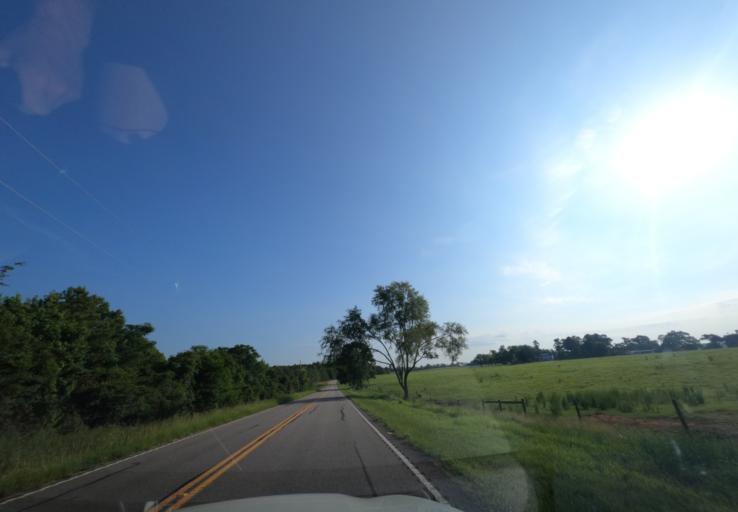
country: US
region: South Carolina
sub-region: Edgefield County
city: Murphys Estates
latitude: 33.6096
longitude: -81.9682
